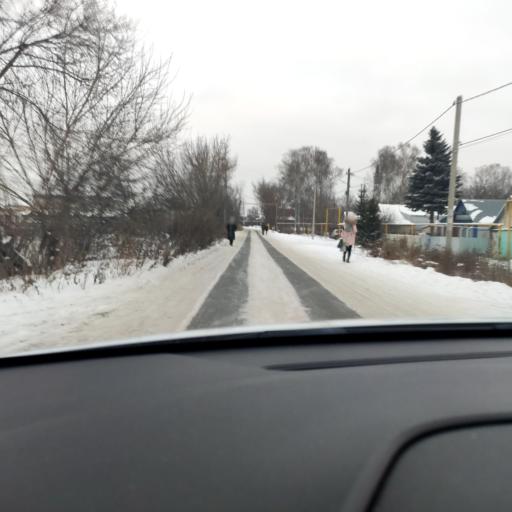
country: RU
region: Tatarstan
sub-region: Gorod Kazan'
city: Kazan
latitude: 55.8742
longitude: 49.1497
